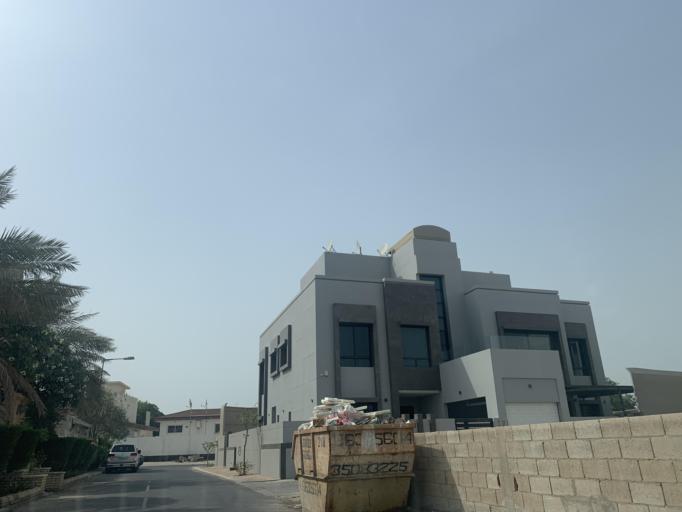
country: BH
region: Manama
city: Jidd Hafs
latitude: 26.2003
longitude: 50.4813
